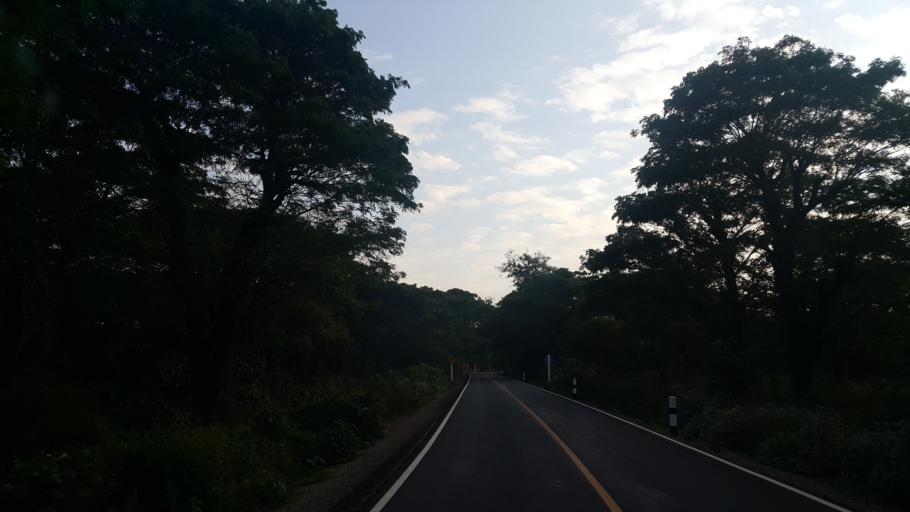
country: TH
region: Lampang
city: Sop Prap
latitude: 17.9315
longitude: 99.3385
